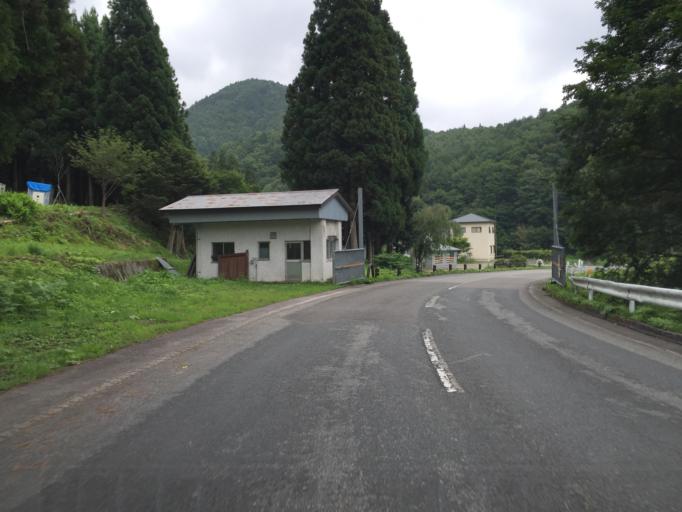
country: JP
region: Fukushima
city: Inawashiro
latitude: 37.6570
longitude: 140.1609
